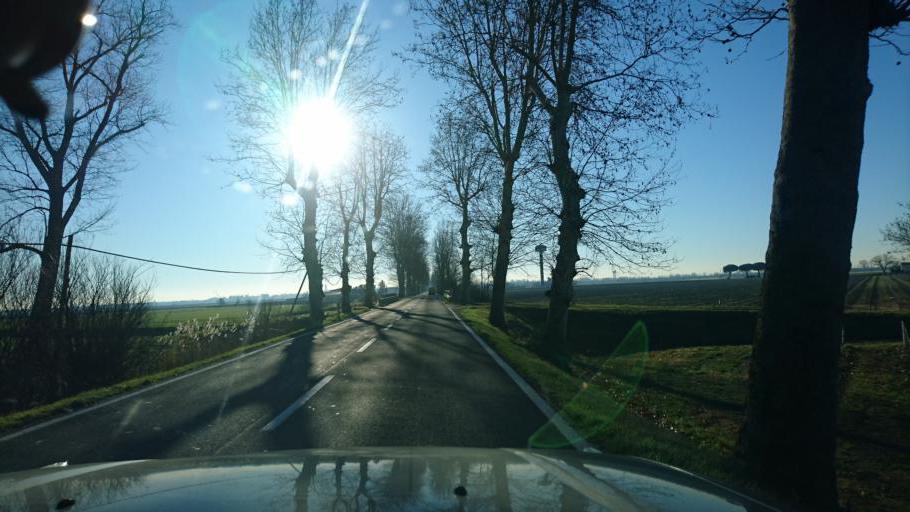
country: IT
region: Veneto
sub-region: Provincia di Venezia
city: Cavarzere
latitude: 45.1566
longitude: 12.0542
